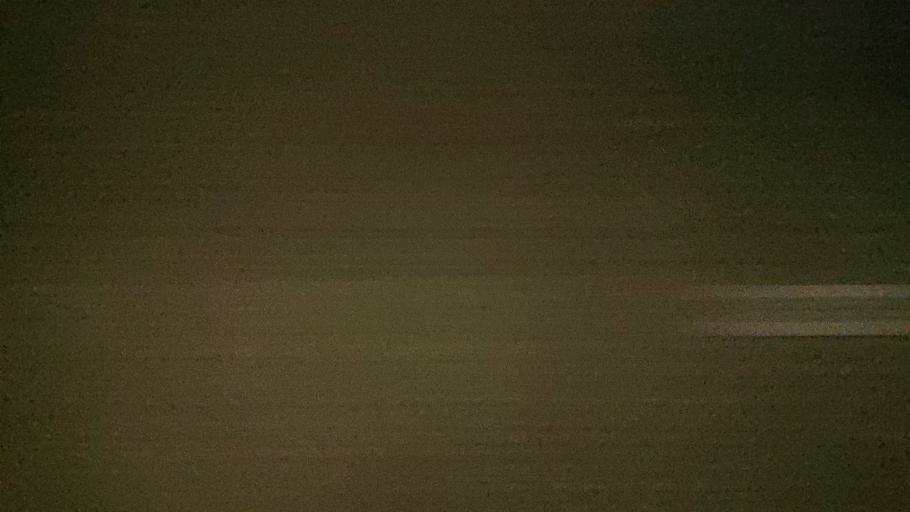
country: TW
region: Taiwan
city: Lugu
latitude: 23.8273
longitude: 120.7622
